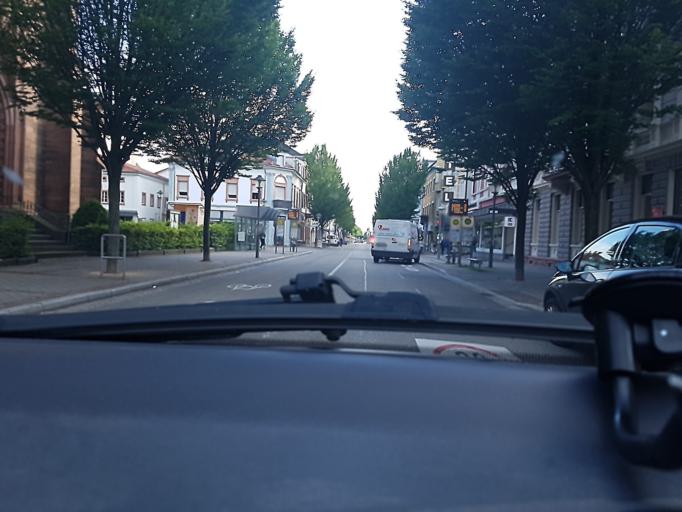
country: DE
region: Baden-Wuerttemberg
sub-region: Freiburg Region
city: Offenburg
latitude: 48.4726
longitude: 7.9435
